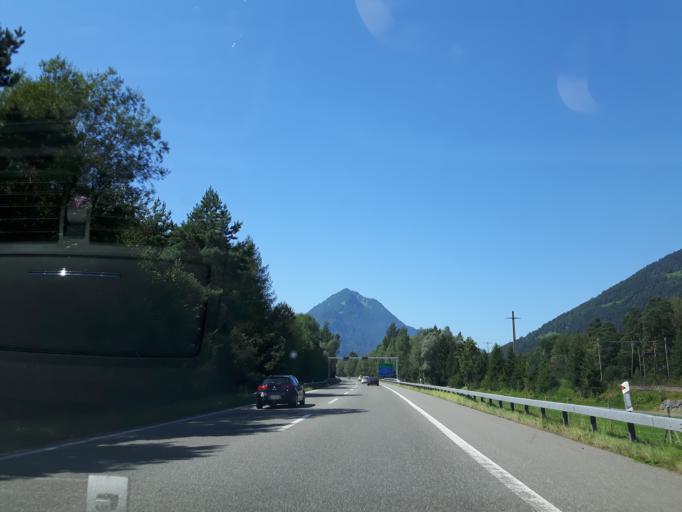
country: CH
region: Saint Gallen
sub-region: Wahlkreis See-Gaster
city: Weesen
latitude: 47.1267
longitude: 9.1090
